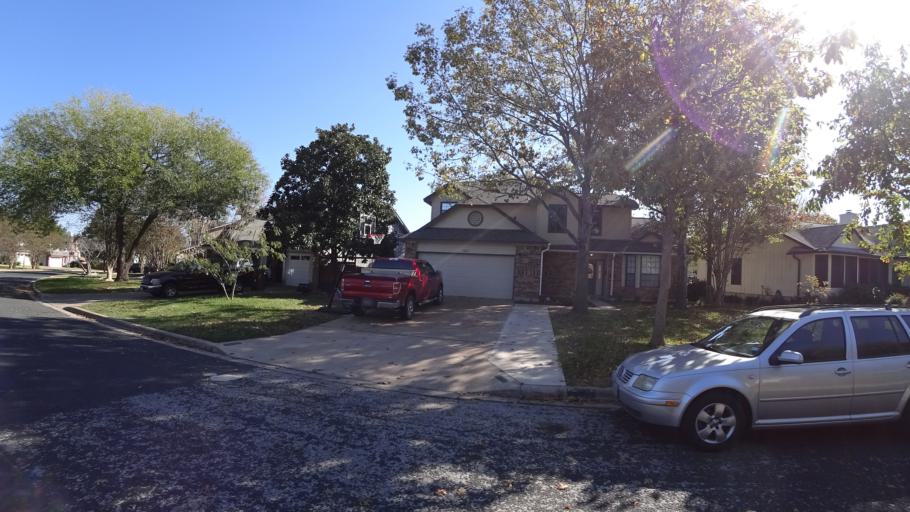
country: US
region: Texas
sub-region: Travis County
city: Shady Hollow
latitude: 30.2237
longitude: -97.8664
